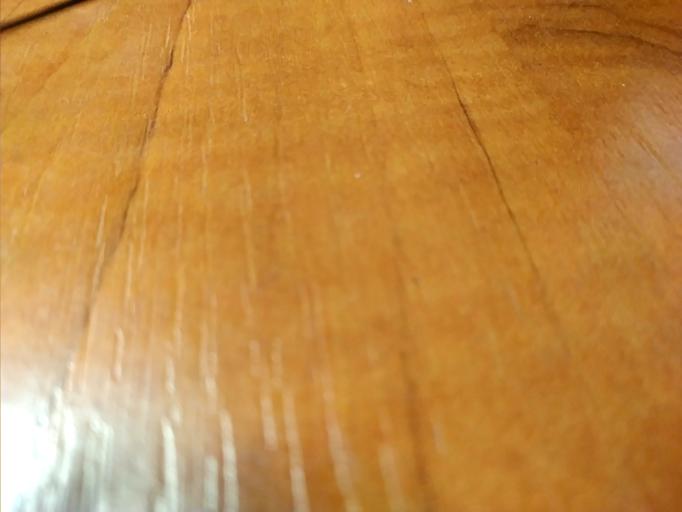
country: RU
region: Tverskaya
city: Rameshki
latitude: 57.1313
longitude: 36.1090
